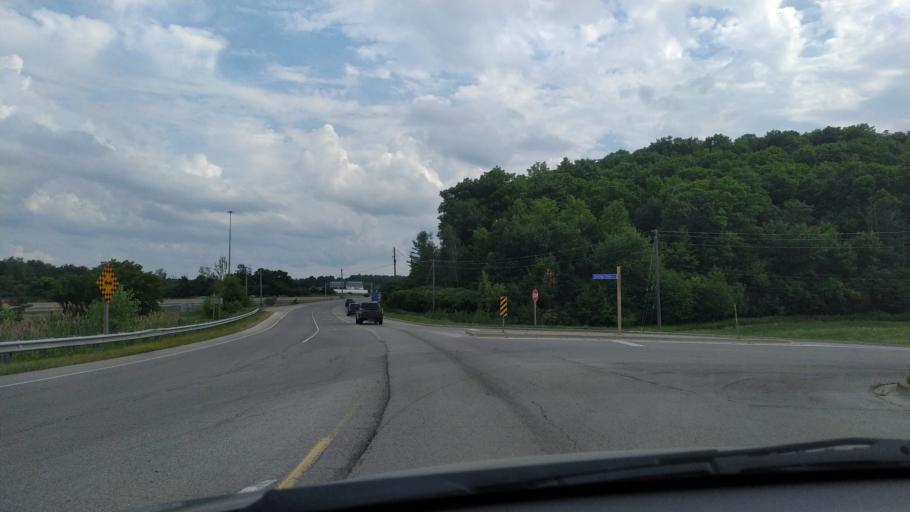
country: CA
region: Ontario
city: Cambridge
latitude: 43.3844
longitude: -80.4075
